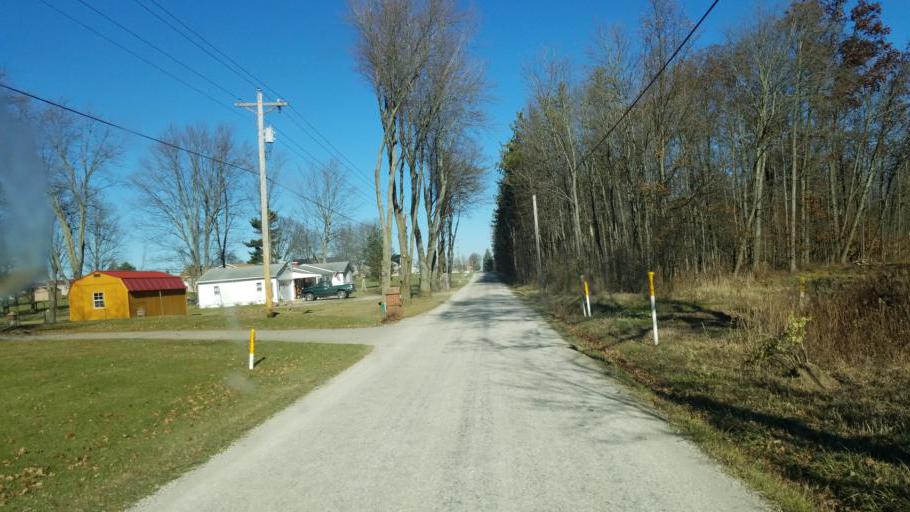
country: US
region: Ohio
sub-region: Ashland County
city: Ashland
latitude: 40.8637
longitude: -82.3876
